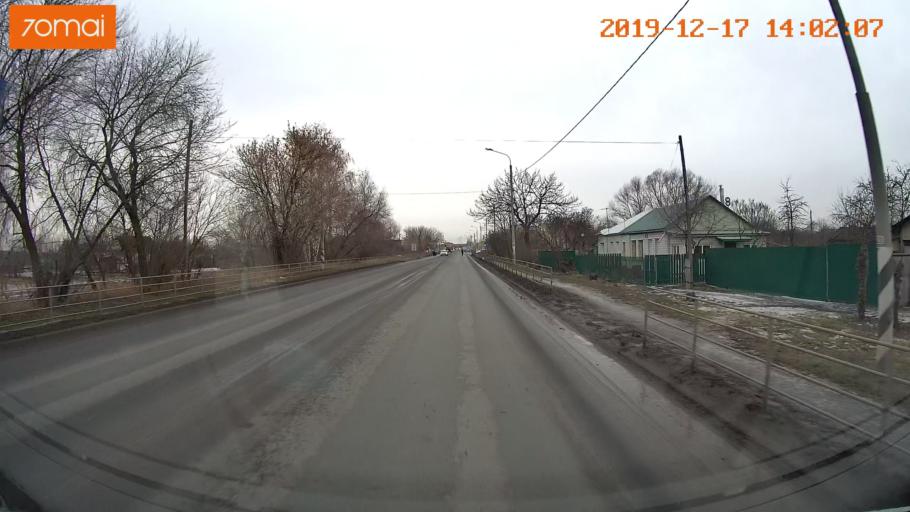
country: RU
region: Rjazan
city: Ryazan'
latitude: 54.6160
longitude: 39.6502
